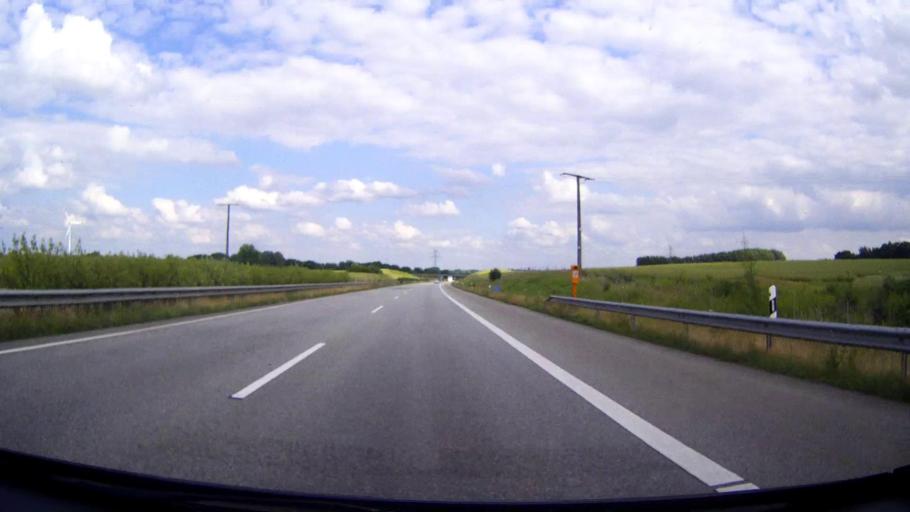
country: DE
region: Schleswig-Holstein
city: Monkhagen
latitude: 53.9134
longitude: 10.5420
